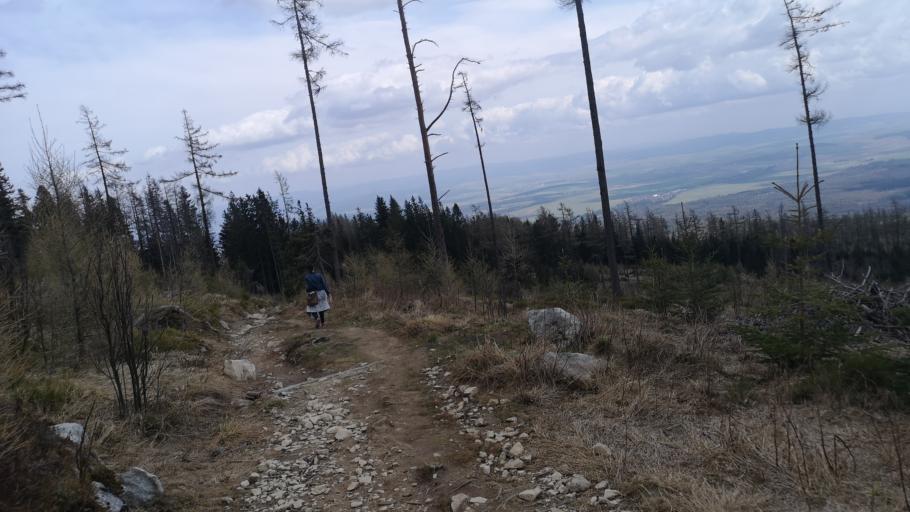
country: SK
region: Presovsky
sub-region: Okres Poprad
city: Vysoke Tatry
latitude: 49.1578
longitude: 20.2200
